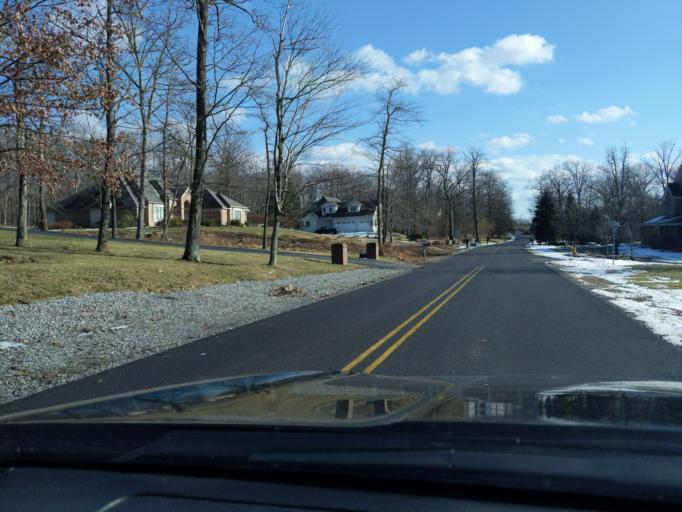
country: US
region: Pennsylvania
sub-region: Blair County
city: Lakemont
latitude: 40.4719
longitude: -78.3738
